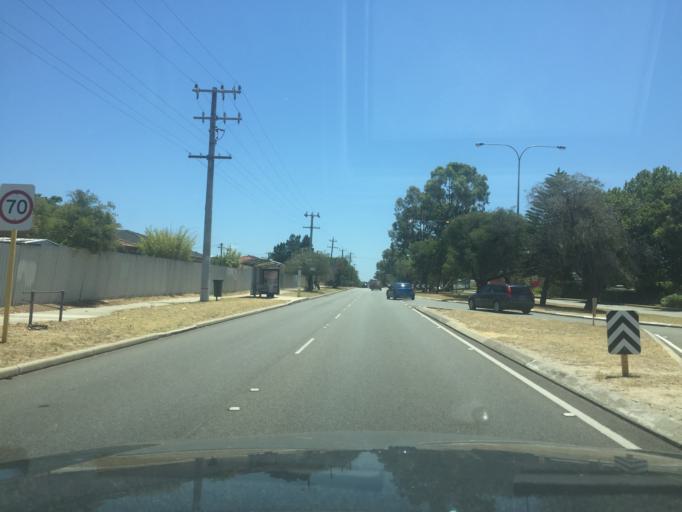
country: AU
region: Western Australia
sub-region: Fremantle
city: Samson
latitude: -32.0657
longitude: 115.8005
